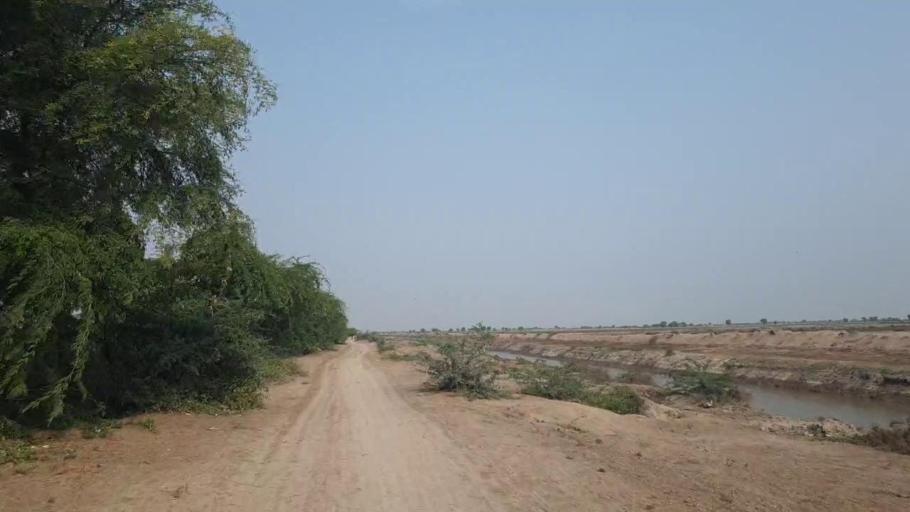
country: PK
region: Sindh
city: Badin
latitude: 24.7191
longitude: 68.7707
